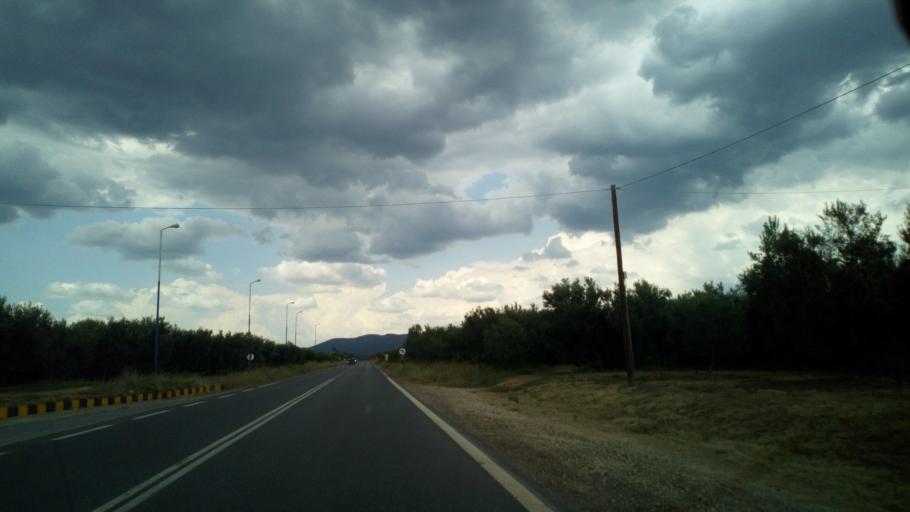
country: GR
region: Central Macedonia
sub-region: Nomos Chalkidikis
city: Kalyves Polygyrou
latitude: 40.2878
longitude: 23.4309
